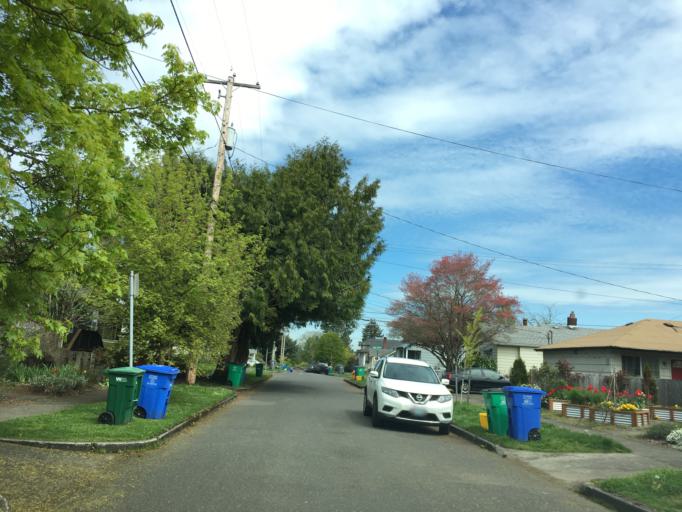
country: US
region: Oregon
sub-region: Multnomah County
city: Lents
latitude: 45.5310
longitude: -122.5888
